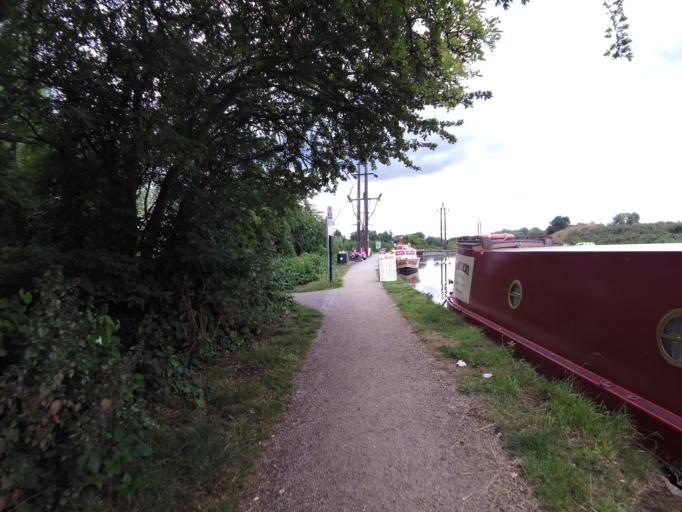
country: GB
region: England
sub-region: Hertfordshire
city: Cheshunt
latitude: 51.7030
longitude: -0.0198
